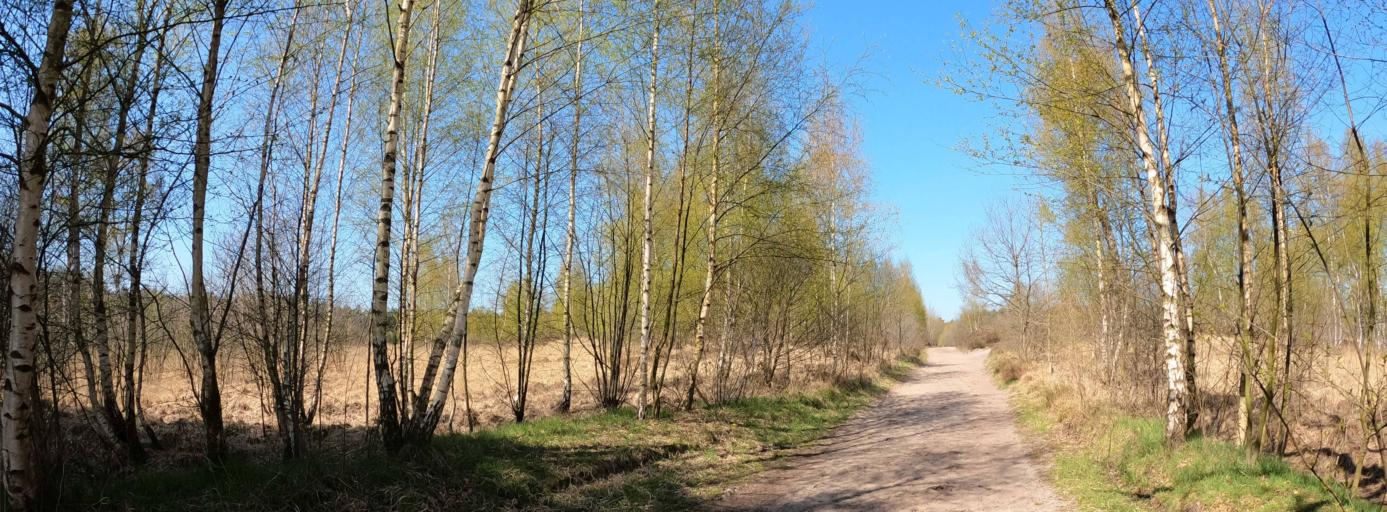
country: BE
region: Flanders
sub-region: Provincie Antwerpen
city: Kalmthout
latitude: 51.3450
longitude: 4.4870
